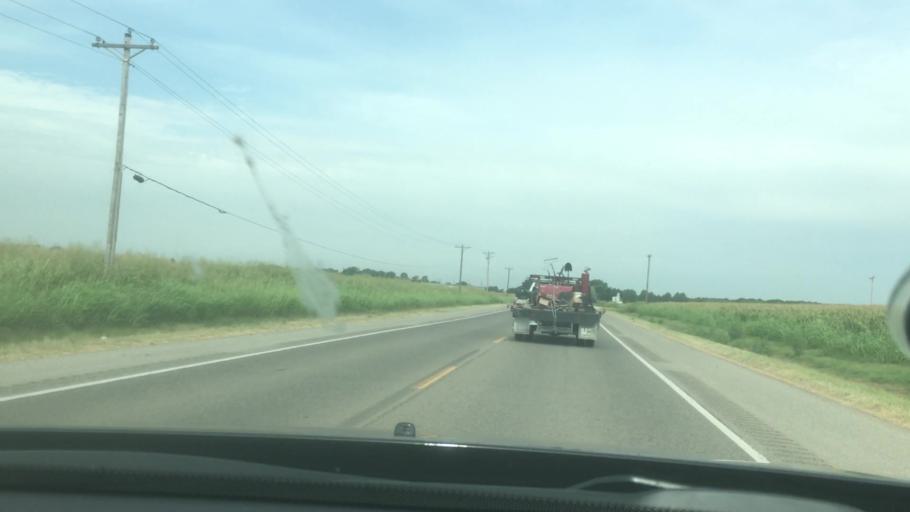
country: US
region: Oklahoma
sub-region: Garvin County
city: Lindsay
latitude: 34.8259
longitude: -97.5484
